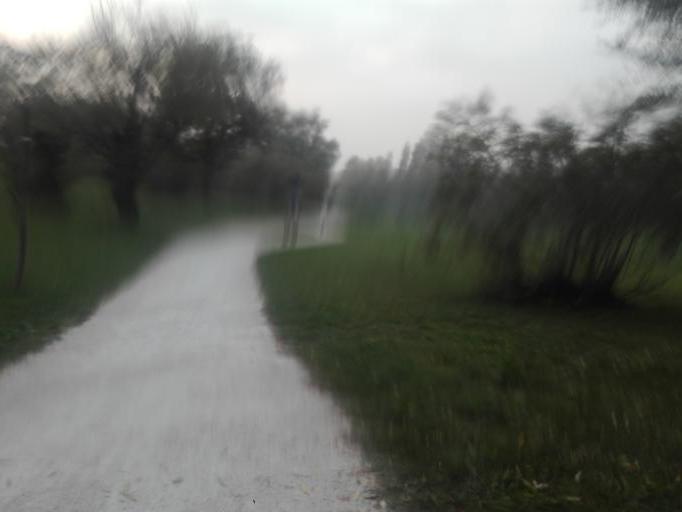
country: IT
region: Emilia-Romagna
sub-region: Provincia di Rimini
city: Rimini
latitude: 44.0632
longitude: 12.5549
